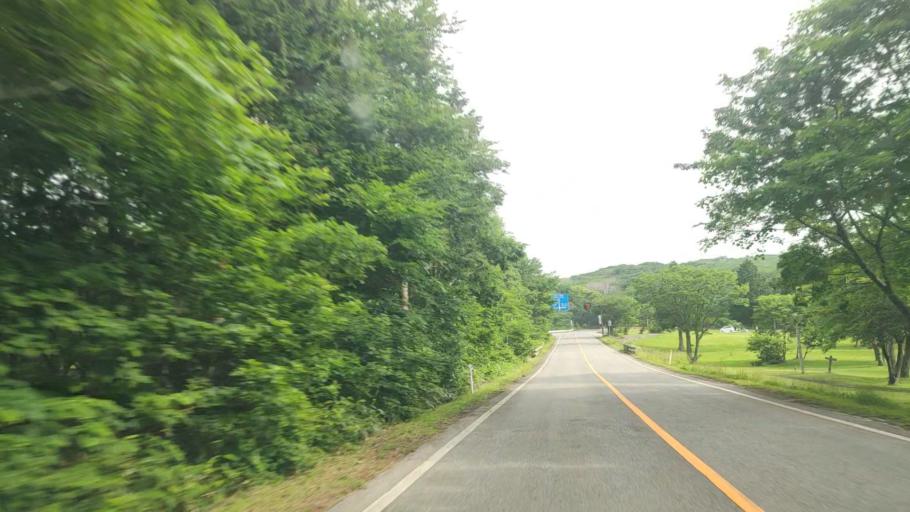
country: JP
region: Tottori
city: Kurayoshi
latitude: 35.3447
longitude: 133.5879
